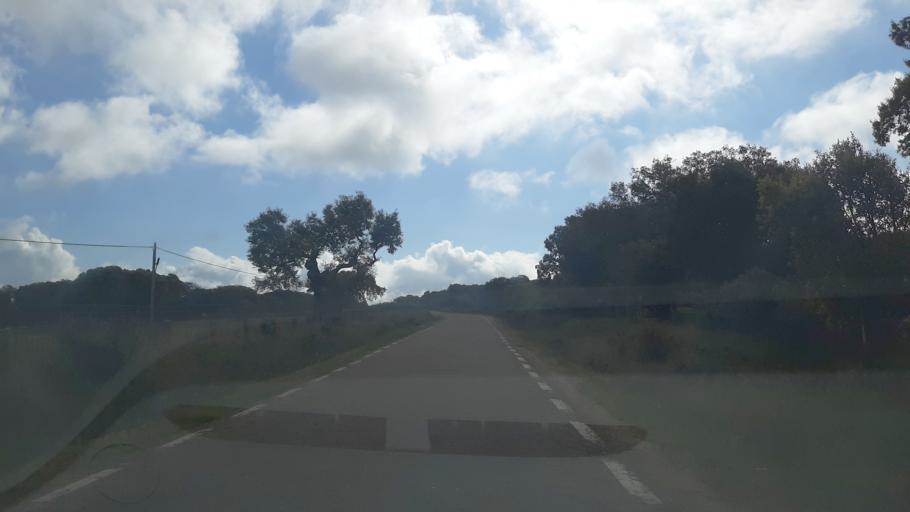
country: ES
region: Castille and Leon
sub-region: Provincia de Salamanca
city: Narros de Matalayegua
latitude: 40.7031
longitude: -5.9110
